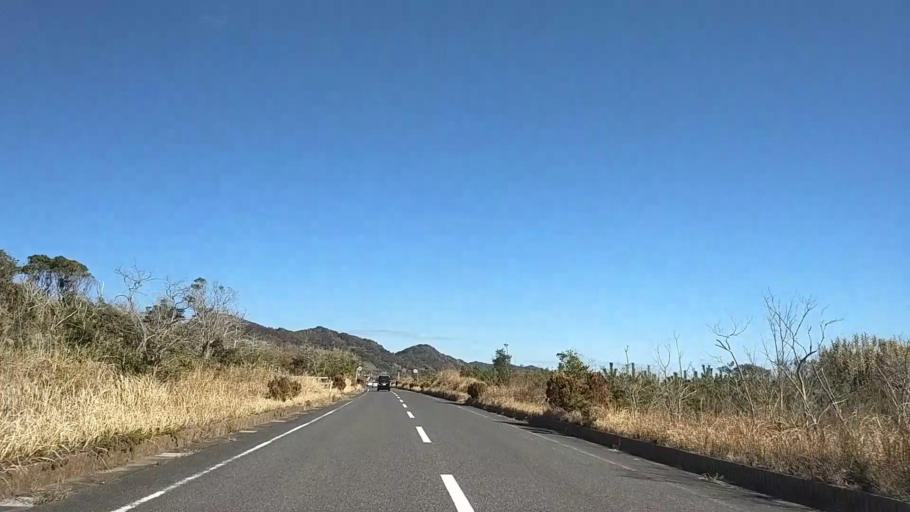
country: JP
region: Chiba
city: Tateyama
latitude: 35.0198
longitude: 139.9881
